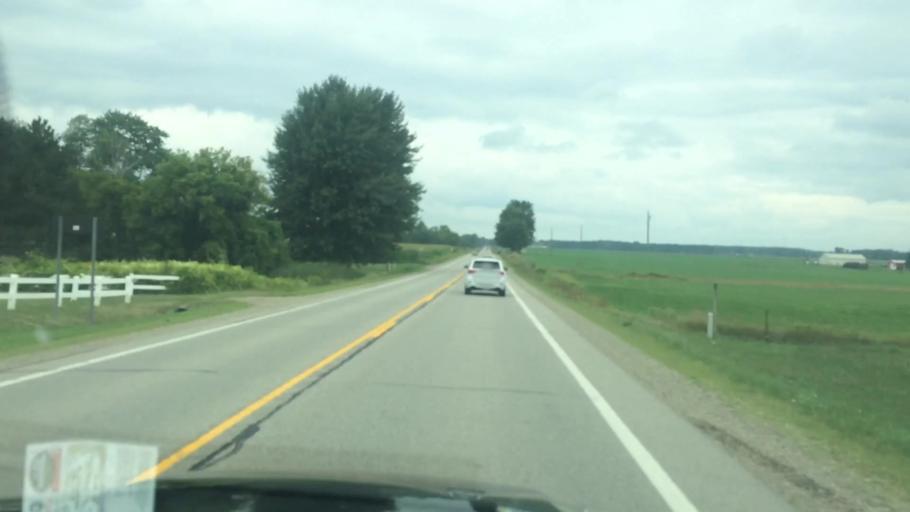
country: US
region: Michigan
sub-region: Sanilac County
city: Marlette
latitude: 43.4675
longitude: -83.0897
